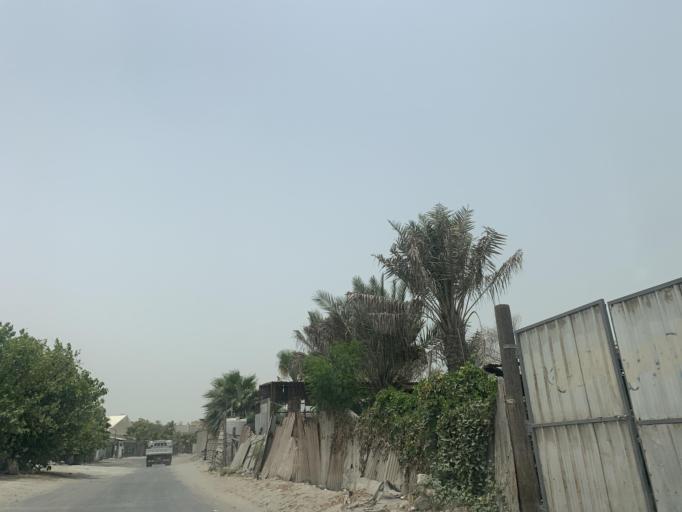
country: BH
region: Manama
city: Jidd Hafs
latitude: 26.2154
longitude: 50.5056
